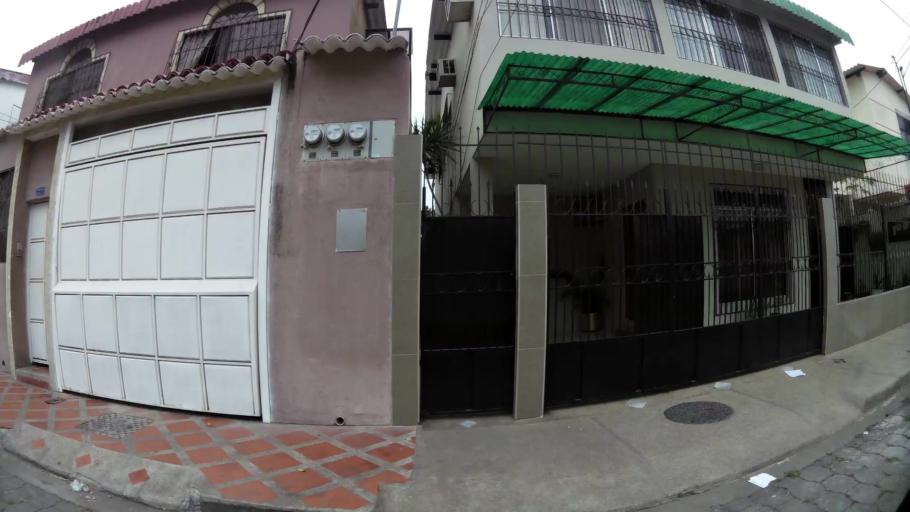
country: EC
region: Guayas
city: Eloy Alfaro
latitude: -2.1375
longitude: -79.9014
